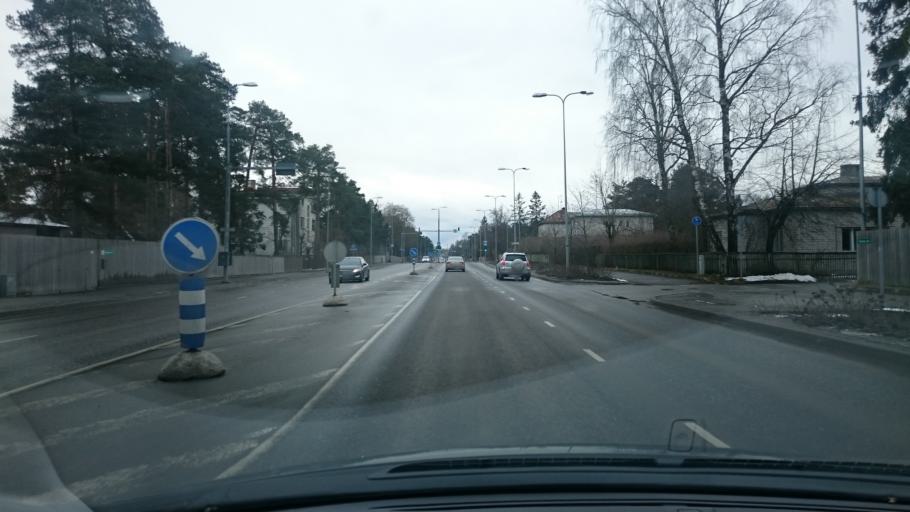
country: EE
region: Harju
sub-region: Tallinna linn
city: Tallinn
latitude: 59.3838
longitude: 24.7175
